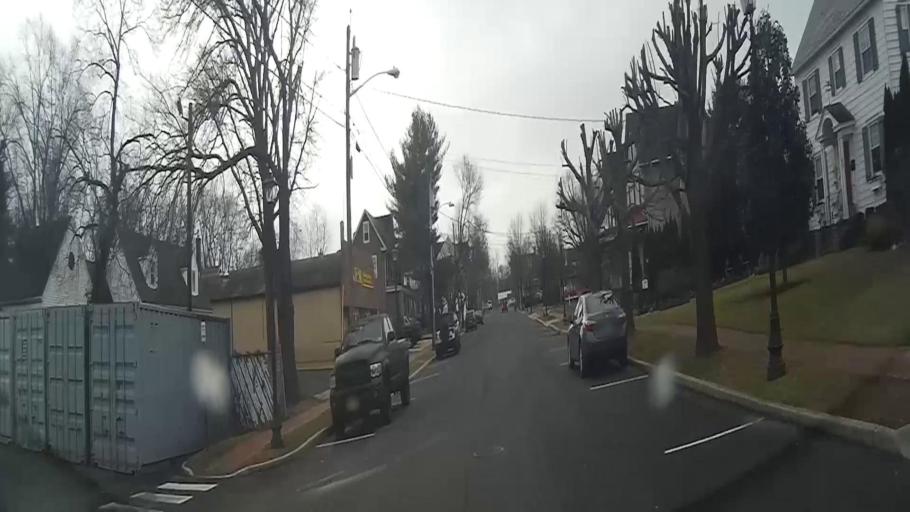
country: US
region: New Jersey
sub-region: Burlington County
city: Marlton
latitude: 39.8924
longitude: -74.9189
